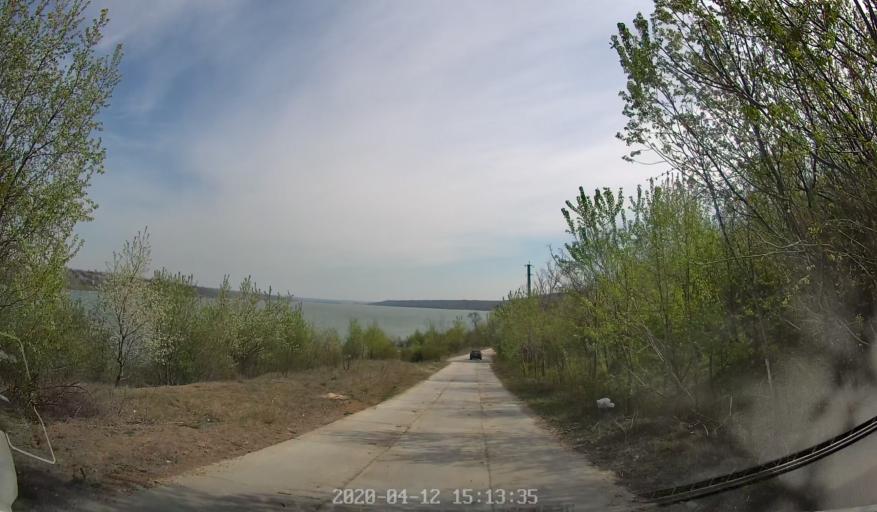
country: MD
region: Telenesti
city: Cocieri
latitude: 47.3266
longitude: 29.0735
